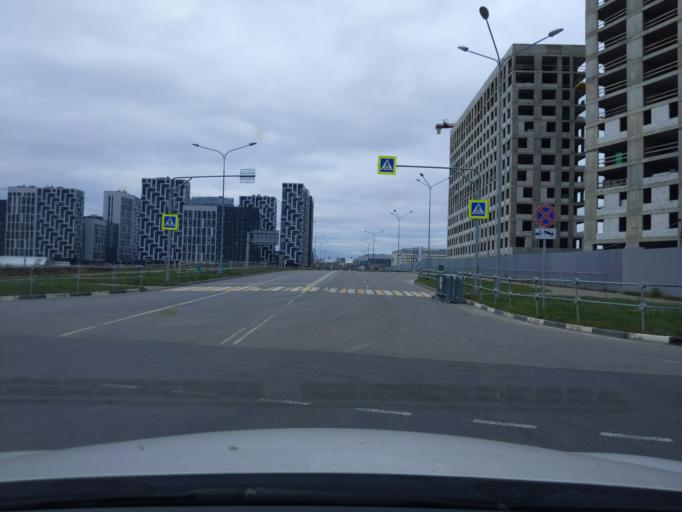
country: RU
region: Moscow
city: Pokrovskoye-Streshnevo
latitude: 55.8210
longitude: 37.4393
